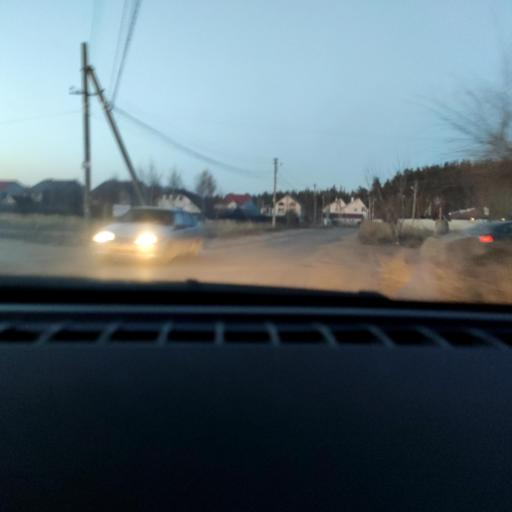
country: RU
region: Voronezj
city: Podgornoye
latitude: 51.7444
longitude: 39.1613
